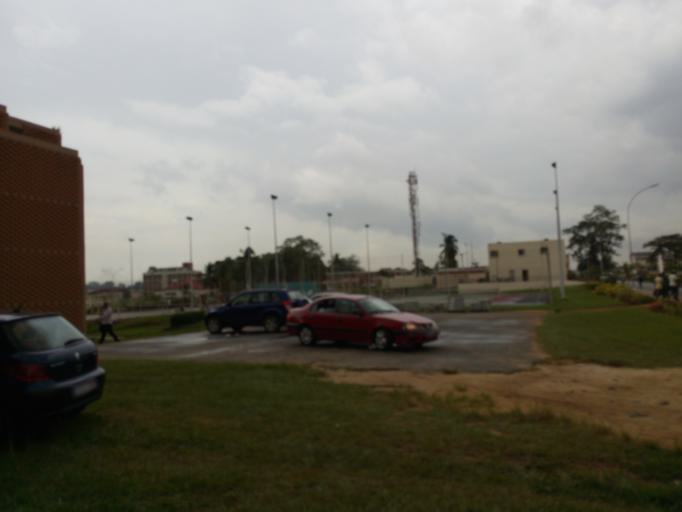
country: CI
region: Lagunes
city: Abidjan
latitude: 5.3414
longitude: -3.9879
